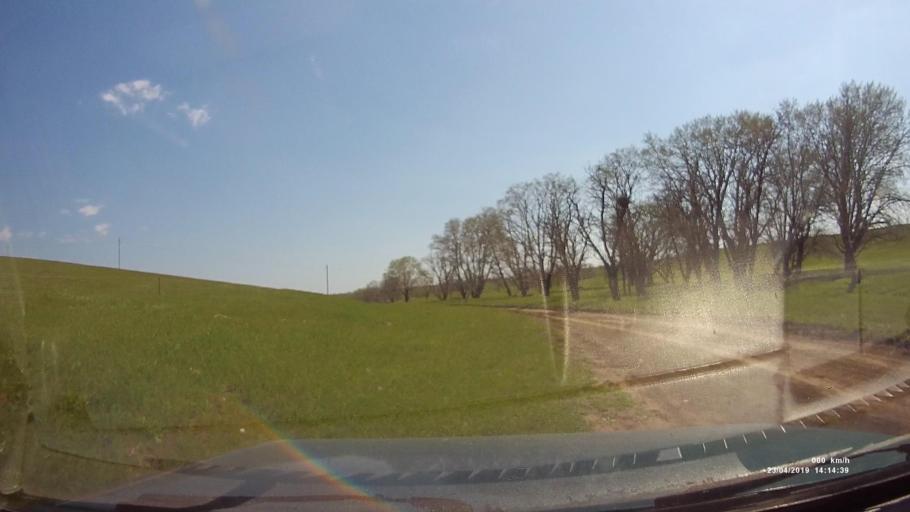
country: RU
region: Rostov
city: Remontnoye
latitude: 46.5569
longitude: 42.9475
